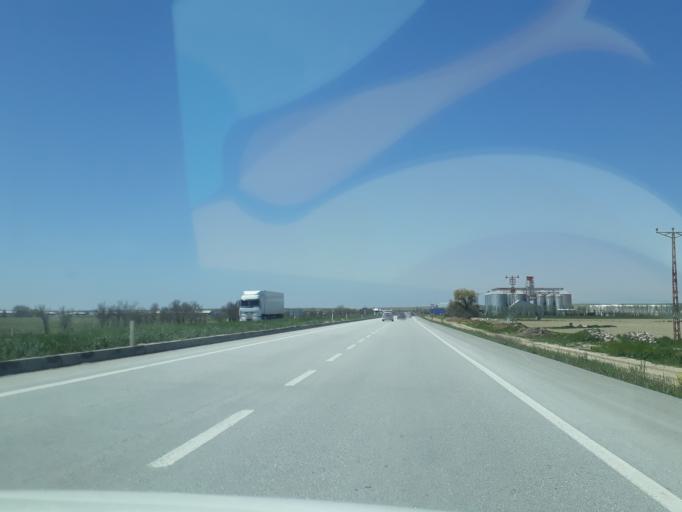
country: TR
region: Konya
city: Karapinar
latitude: 37.7152
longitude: 33.5095
